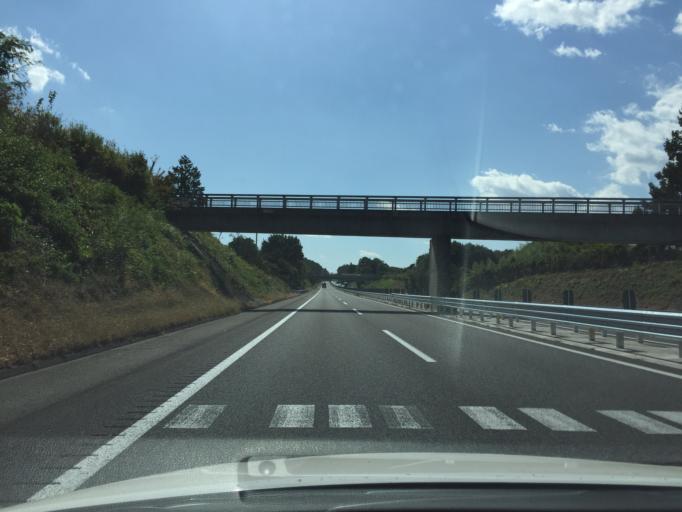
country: JP
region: Fukushima
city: Sukagawa
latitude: 37.2434
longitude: 140.3298
